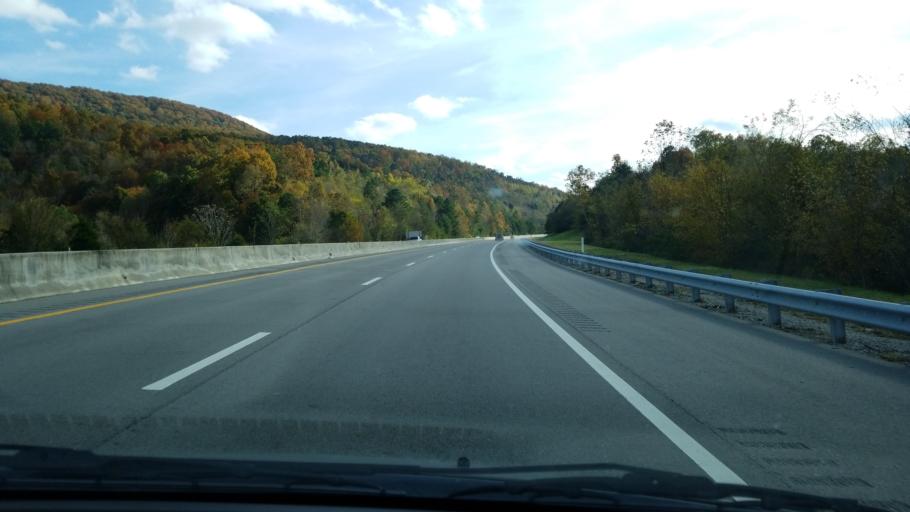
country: US
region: Tennessee
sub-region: Sequatchie County
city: Dunlap
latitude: 35.3857
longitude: -85.3308
